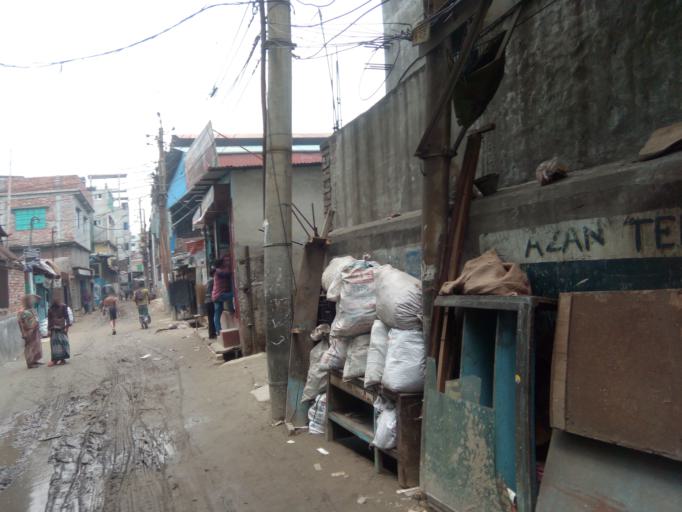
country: BD
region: Dhaka
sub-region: Dhaka
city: Dhaka
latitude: 23.6864
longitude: 90.4366
